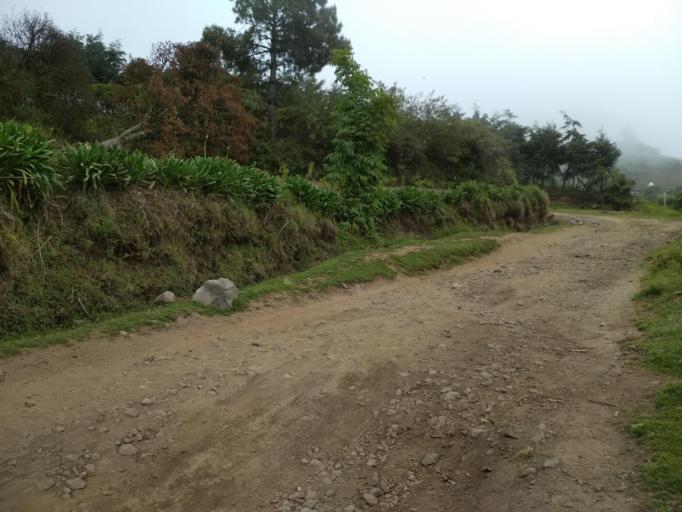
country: MX
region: Veracruz
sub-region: Mariano Escobedo
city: Texmola
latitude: 18.9609
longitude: -97.2193
